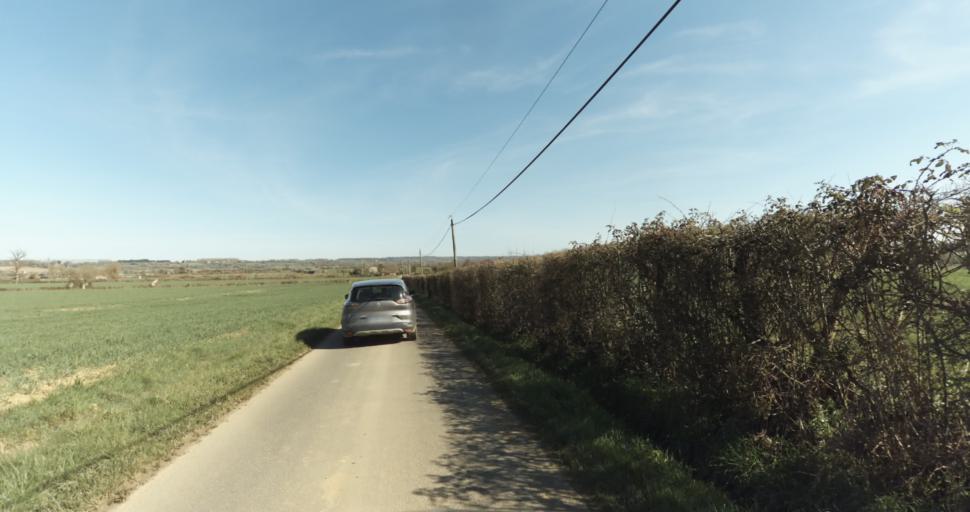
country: FR
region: Lower Normandy
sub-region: Departement du Calvados
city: Saint-Pierre-sur-Dives
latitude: 49.0489
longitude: -0.0174
